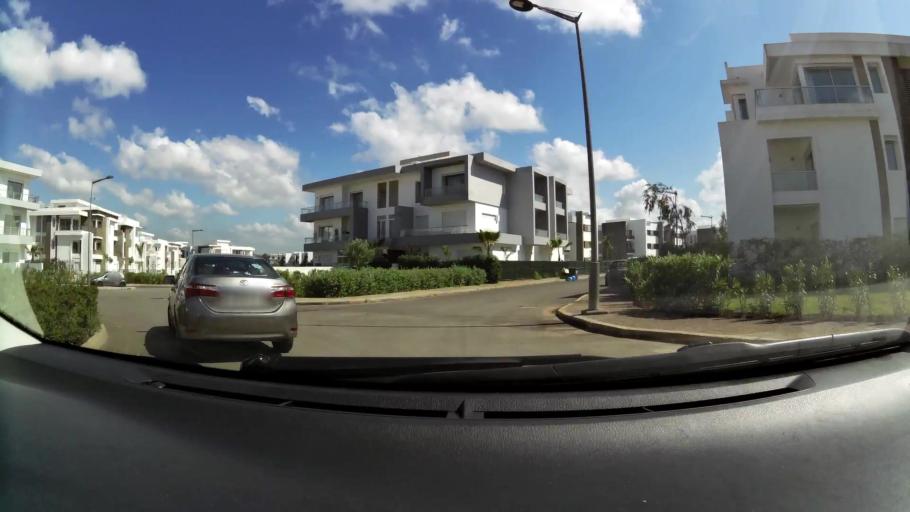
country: MA
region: Grand Casablanca
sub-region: Nouaceur
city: Bouskoura
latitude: 33.4744
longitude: -7.6049
